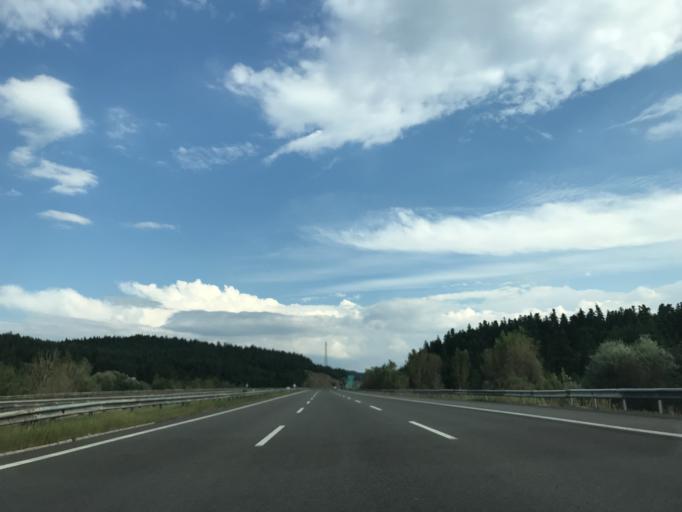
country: TR
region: Bolu
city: Gerede
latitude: 40.6215
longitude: 32.2403
